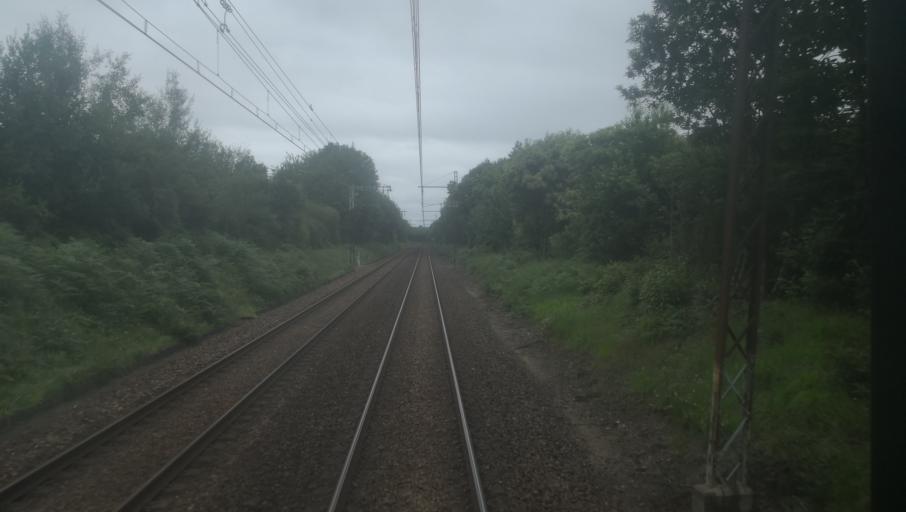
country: FR
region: Centre
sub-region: Departement de l'Indre
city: Chantome
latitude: 46.4492
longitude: 1.5515
